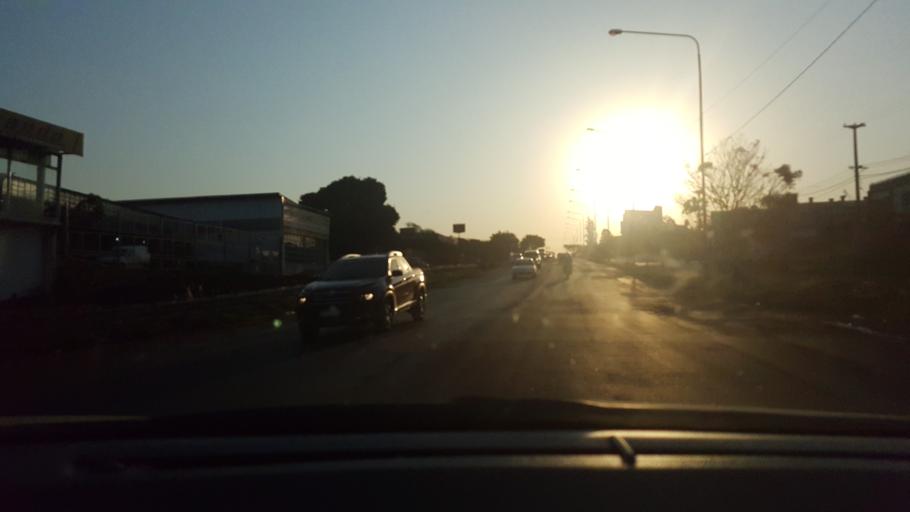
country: AR
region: Misiones
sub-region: Departamento de Capital
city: Posadas
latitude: -27.4044
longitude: -55.9035
